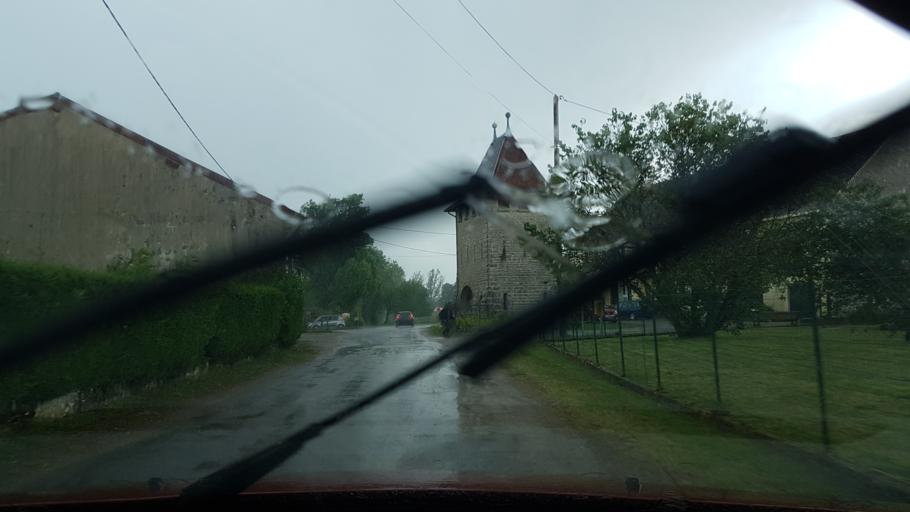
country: FR
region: Franche-Comte
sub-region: Departement du Jura
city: Clairvaux-les-Lacs
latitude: 46.5752
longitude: 5.6935
